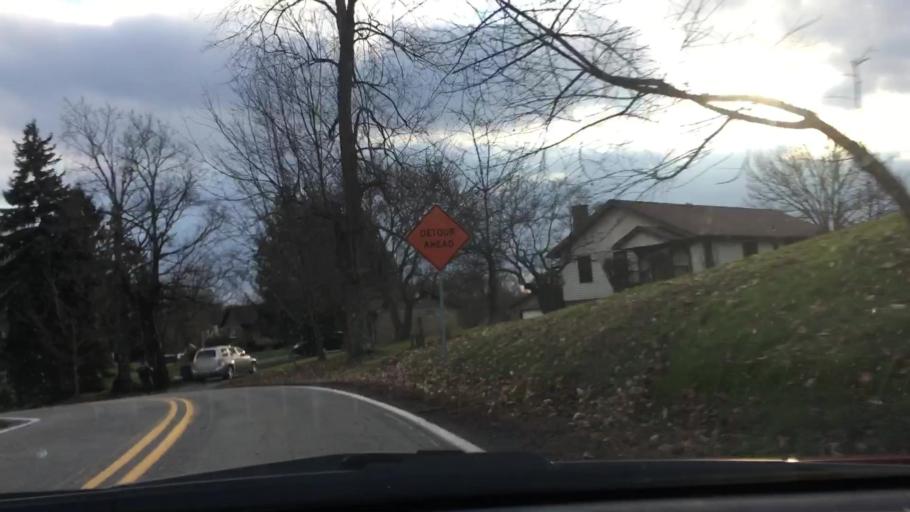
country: US
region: Pennsylvania
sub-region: Allegheny County
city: Lincoln
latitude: 40.3014
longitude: -79.8527
